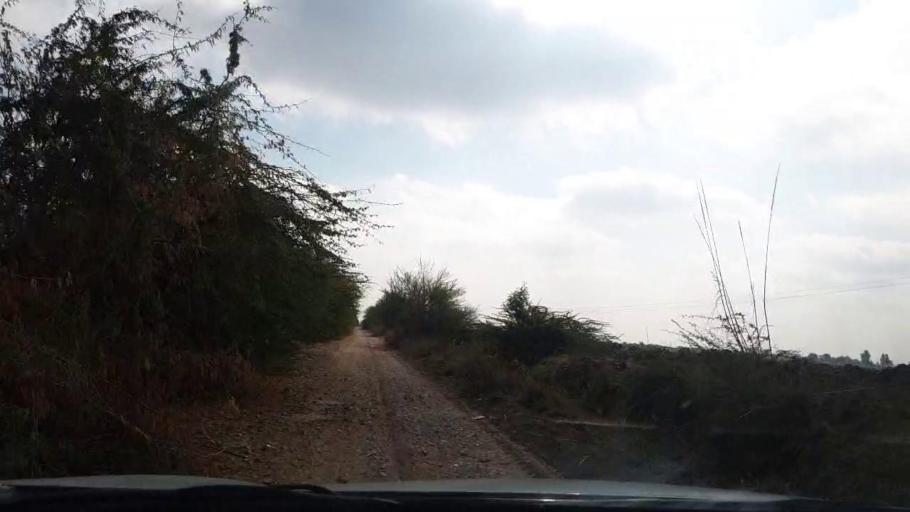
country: PK
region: Sindh
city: Berani
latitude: 25.7785
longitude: 68.9706
